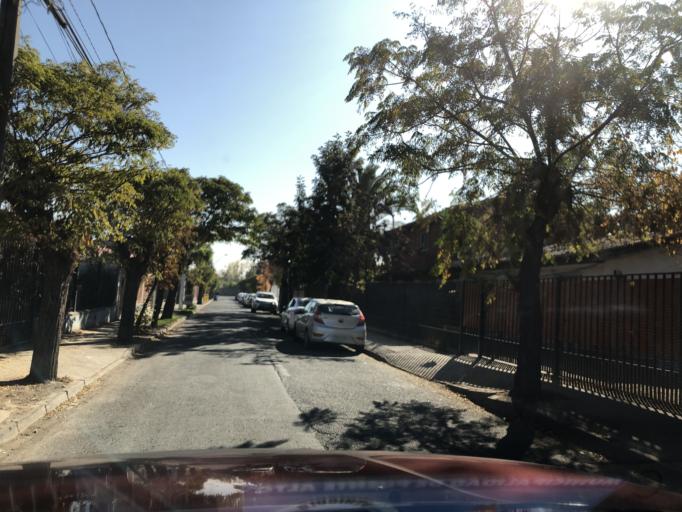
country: CL
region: Santiago Metropolitan
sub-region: Provincia de Cordillera
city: Puente Alto
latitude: -33.5842
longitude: -70.5741
